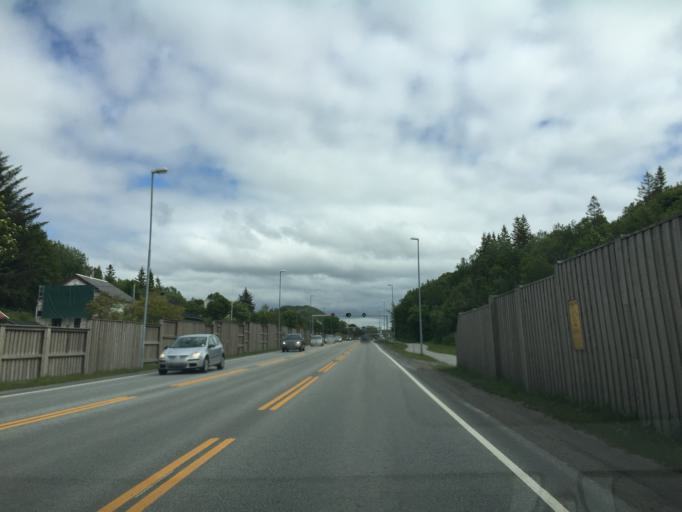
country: NO
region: Nordland
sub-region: Bodo
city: Lopsmarka
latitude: 67.2759
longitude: 14.4473
